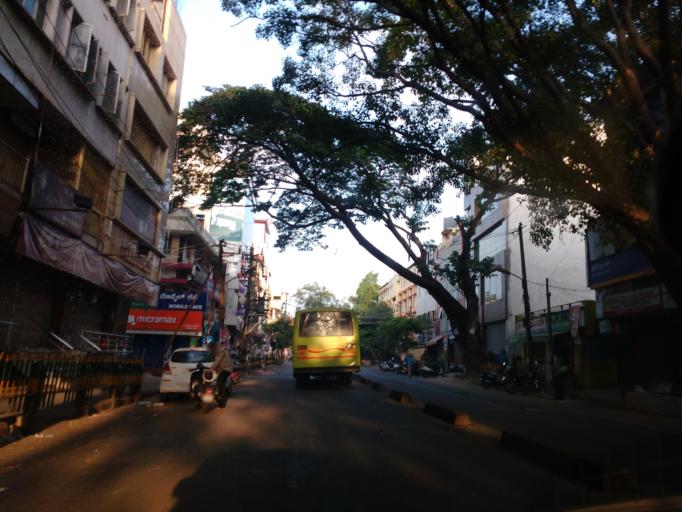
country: IN
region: Karnataka
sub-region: Bangalore Urban
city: Bangalore
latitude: 13.0041
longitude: 77.5513
